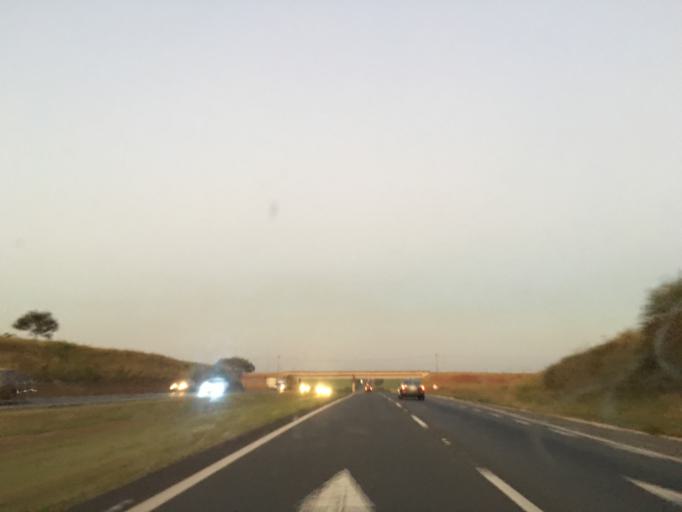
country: BR
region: Sao Paulo
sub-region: Piracicaba
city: Piracicaba
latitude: -22.7236
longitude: -47.5876
